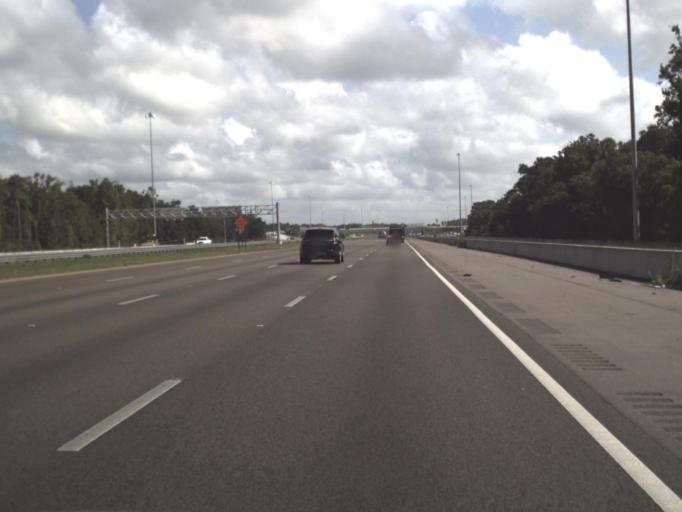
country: US
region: Florida
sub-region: Hillsborough County
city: Pebble Creek
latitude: 28.1852
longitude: -82.3877
